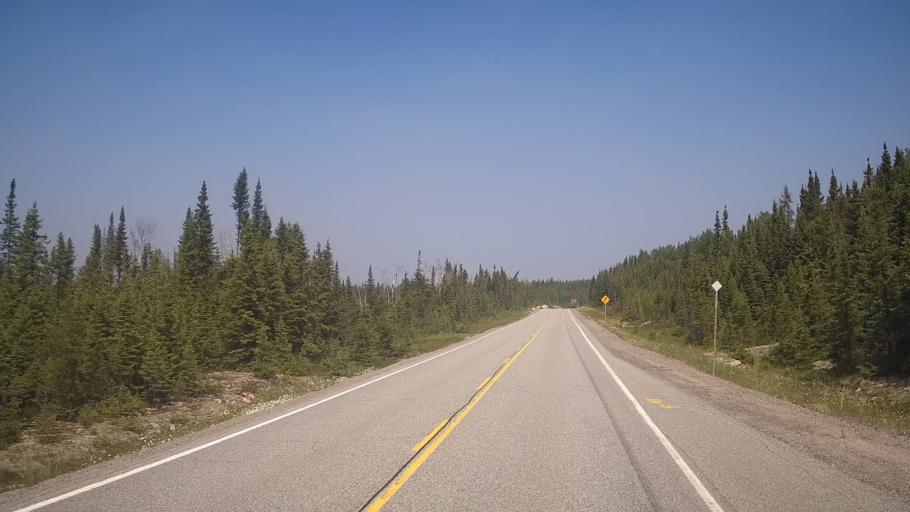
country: CA
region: Ontario
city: Timmins
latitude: 48.0718
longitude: -81.5921
